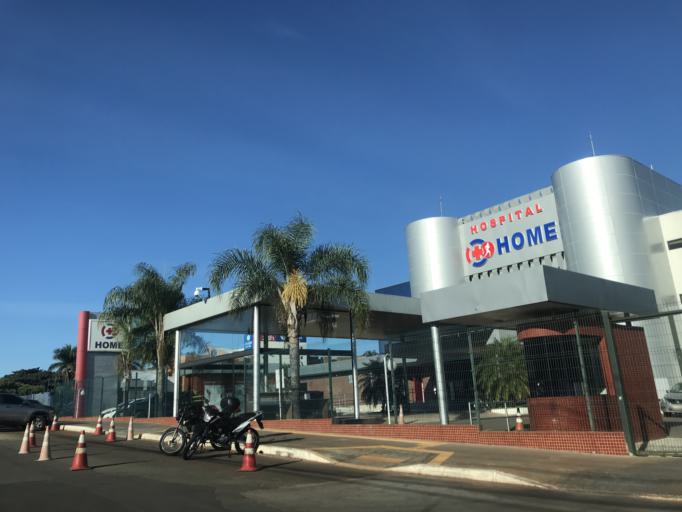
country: BR
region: Federal District
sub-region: Brasilia
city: Brasilia
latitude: -15.8337
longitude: -47.9116
